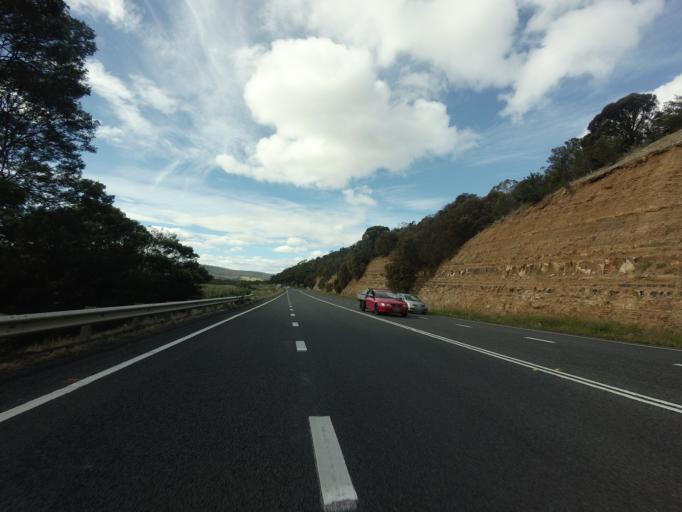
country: AU
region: Tasmania
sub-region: Glenorchy
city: Granton
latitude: -42.7509
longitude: 147.1731
